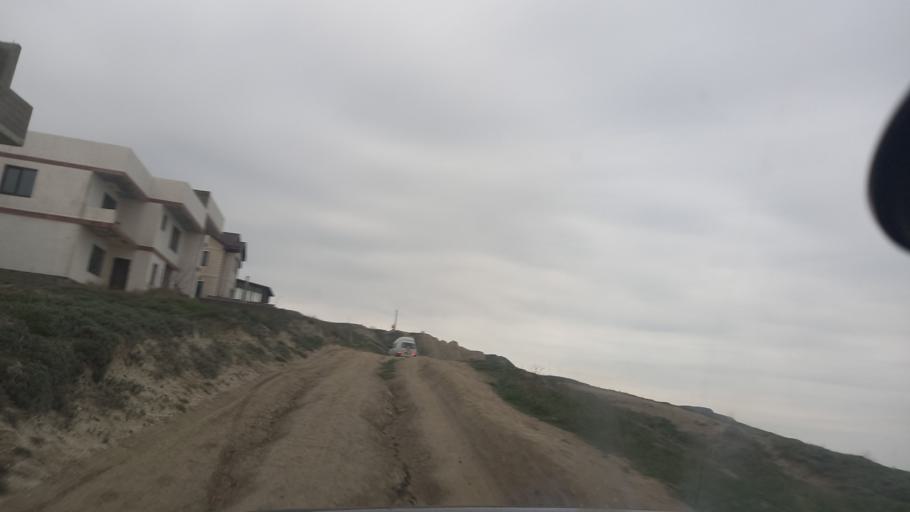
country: RU
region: Krasnodarskiy
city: Anapa
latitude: 44.8540
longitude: 37.3385
